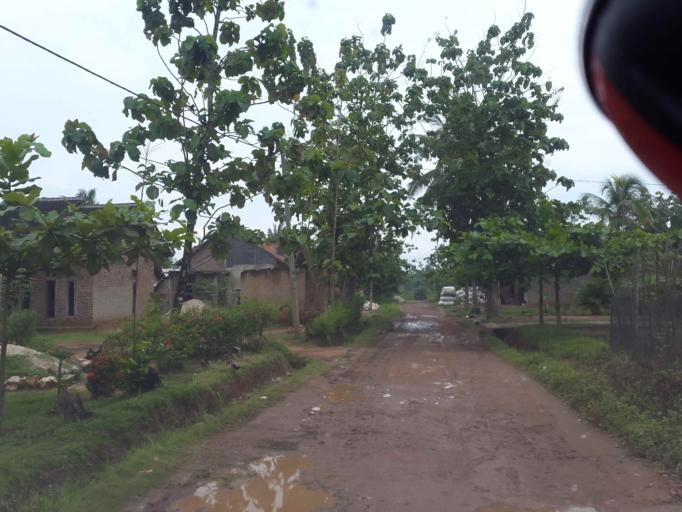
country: ID
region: Lampung
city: Natar
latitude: -5.2381
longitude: 105.1955
